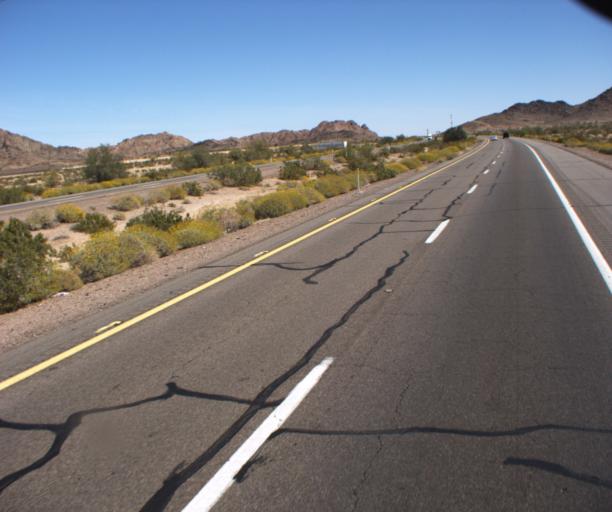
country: US
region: Arizona
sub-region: Yuma County
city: Wellton
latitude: 32.7219
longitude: -113.7650
